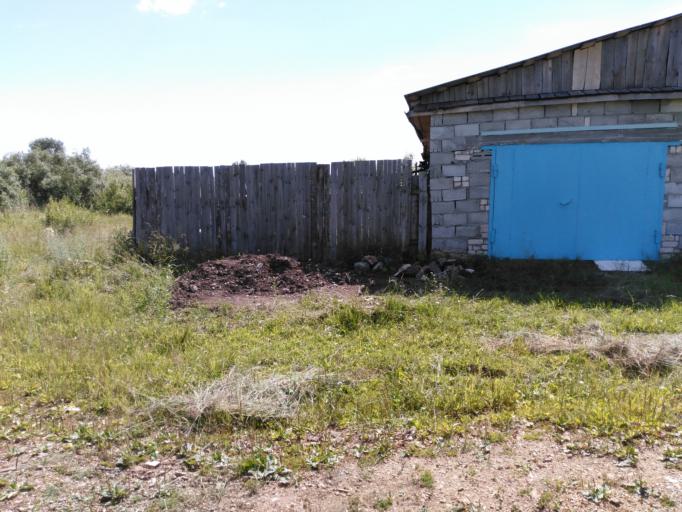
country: RU
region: Bashkortostan
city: Uchaly
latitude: 54.2890
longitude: 59.3646
